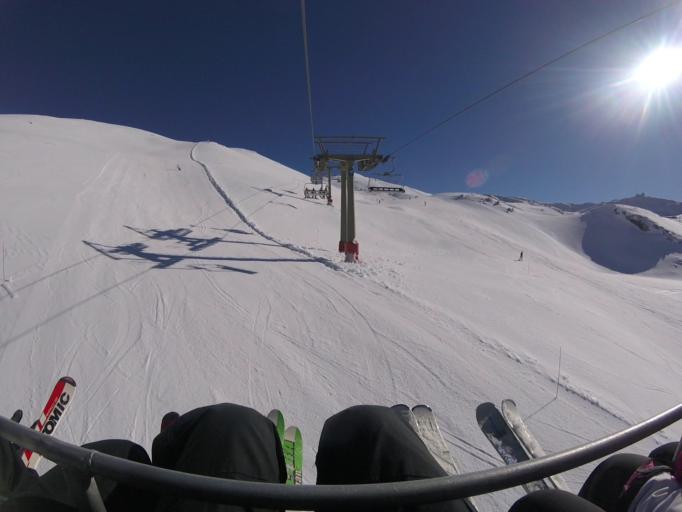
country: ES
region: Andalusia
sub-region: Provincia de Granada
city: Guejar-Sierra
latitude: 37.0723
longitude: -3.3833
